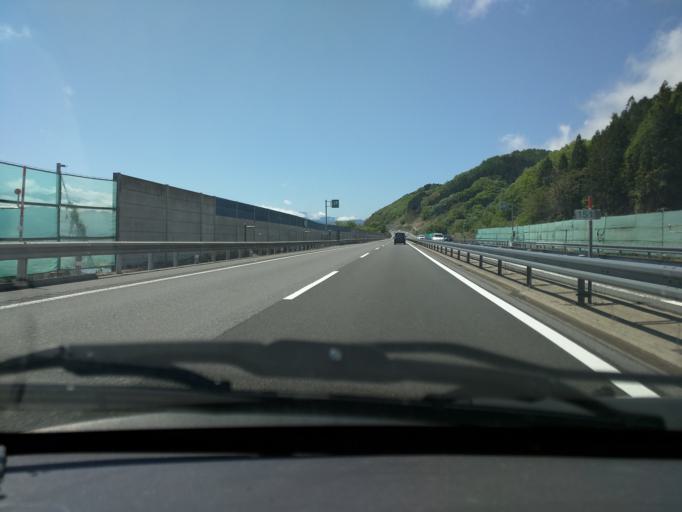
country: JP
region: Nagano
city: Nakano
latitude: 36.7718
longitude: 138.3184
